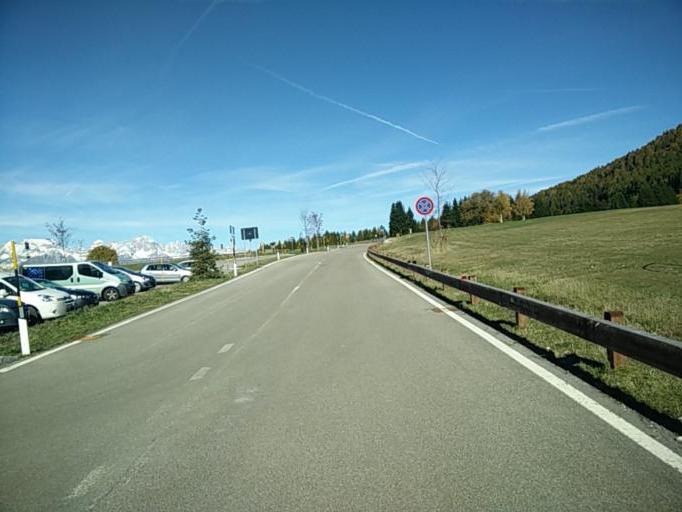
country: IT
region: Trentino-Alto Adige
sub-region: Provincia di Trento
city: Cimoneri
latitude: 46.0203
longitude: 11.0431
